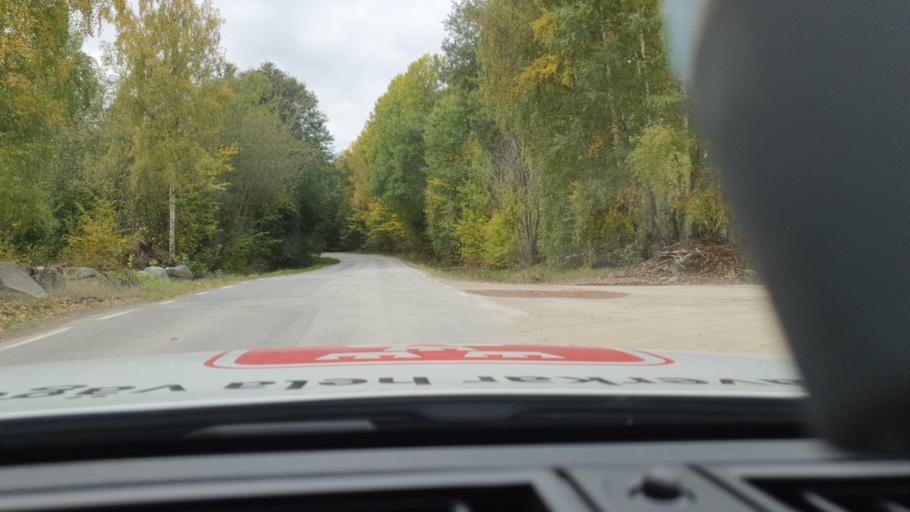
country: SE
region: Stockholm
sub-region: Upplands-Bro Kommun
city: Bro
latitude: 59.4929
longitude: 17.5689
